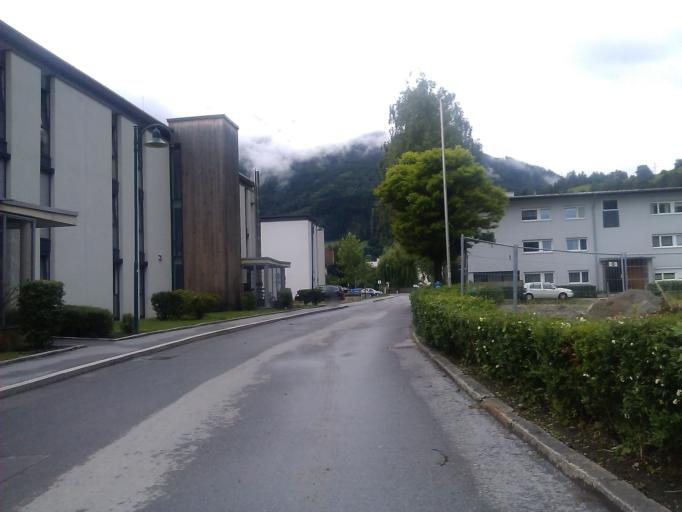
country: AT
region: Tyrol
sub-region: Politischer Bezirk Landeck
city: Landeck
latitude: 47.1514
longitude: 10.5708
